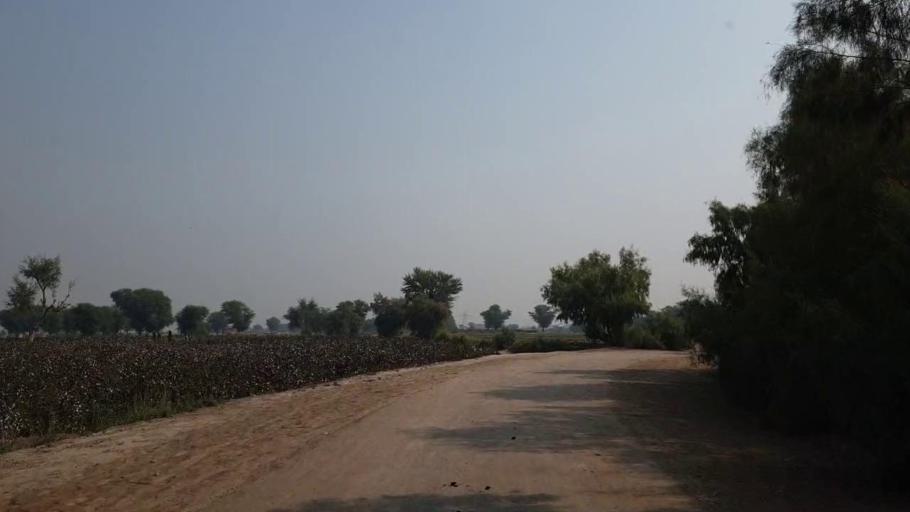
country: PK
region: Sindh
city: Bhan
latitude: 26.5176
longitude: 67.7381
